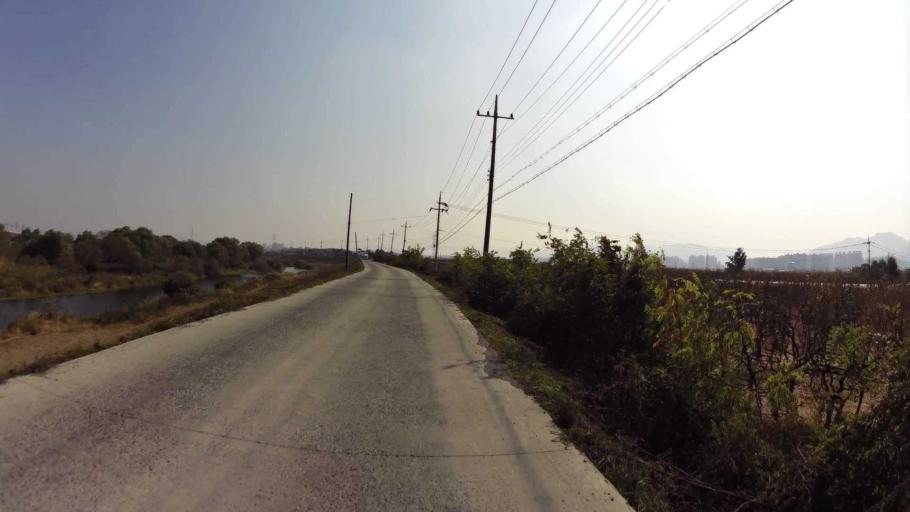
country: KR
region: Gyeongsangbuk-do
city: Gyeongsan-si
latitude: 35.8525
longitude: 128.7320
